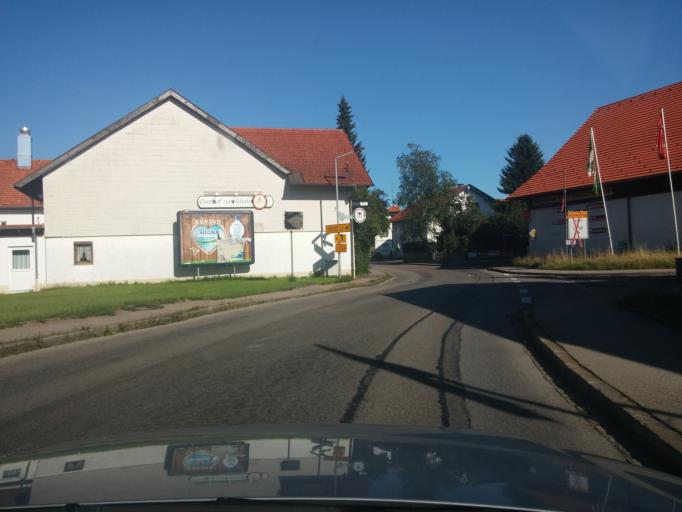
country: DE
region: Bavaria
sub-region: Swabia
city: Altusried
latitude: 47.7971
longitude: 10.1561
